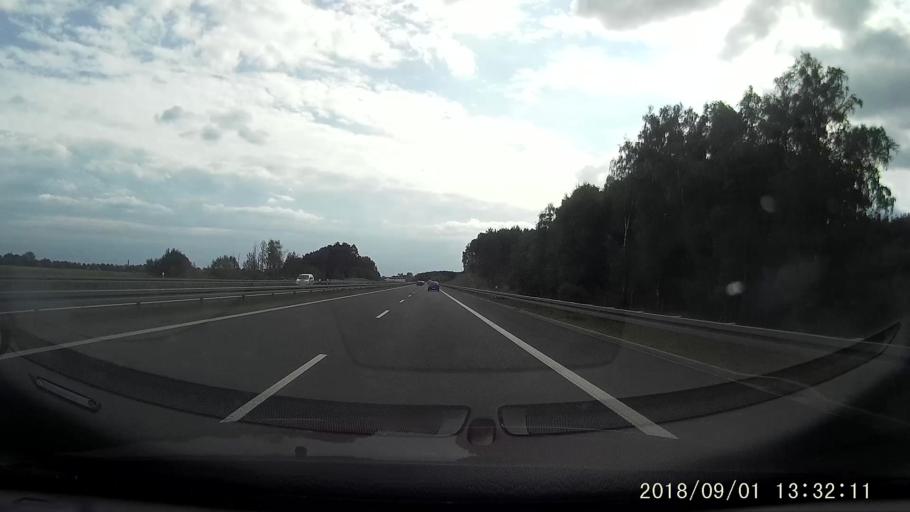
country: PL
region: West Pomeranian Voivodeship
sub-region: Powiat mysliborski
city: Mysliborz
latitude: 53.0029
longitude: 14.8618
